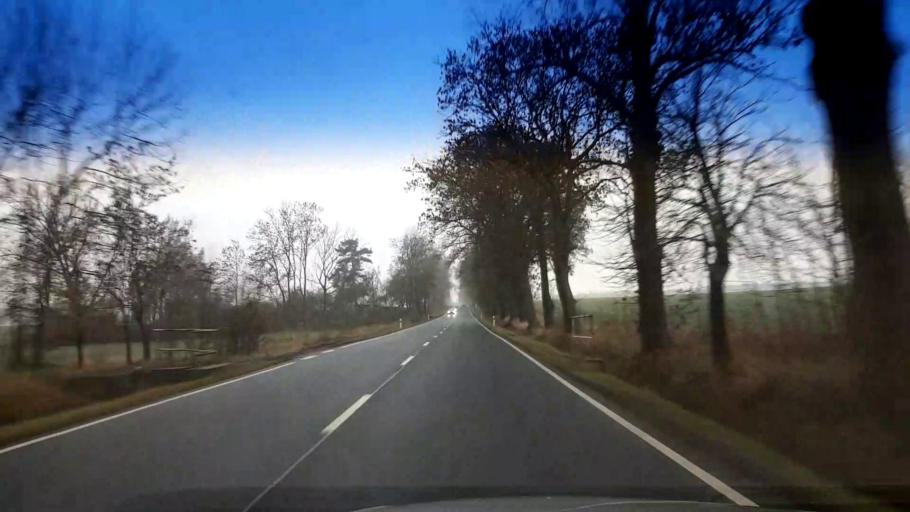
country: CZ
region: Karlovarsky
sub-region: Okres Cheb
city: Cheb
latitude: 50.0586
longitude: 12.3581
